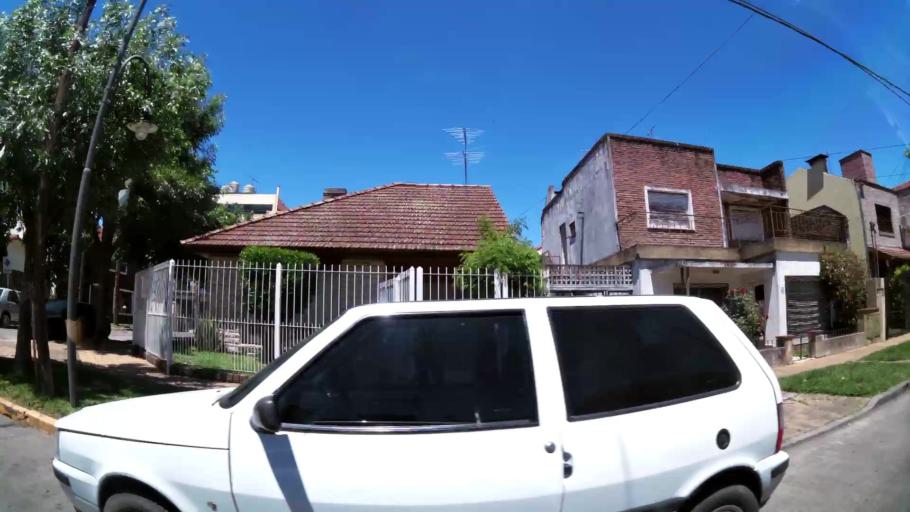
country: AR
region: Buenos Aires
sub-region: Partido de Tigre
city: Tigre
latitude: -34.4453
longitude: -58.5470
